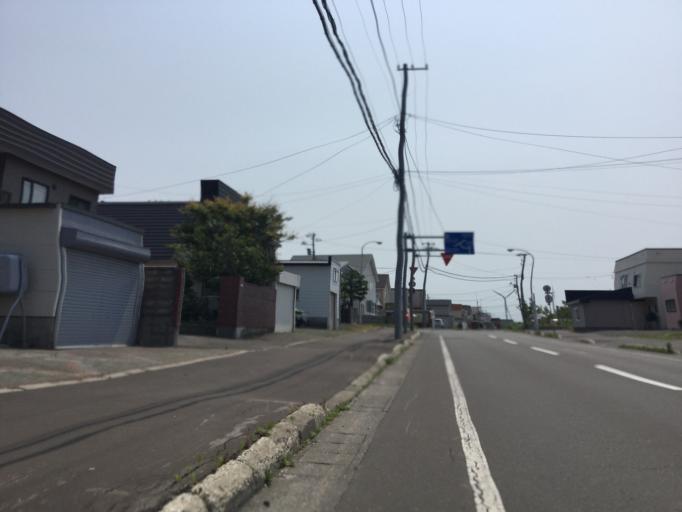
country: JP
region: Hokkaido
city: Wakkanai
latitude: 45.3860
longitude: 141.7227
